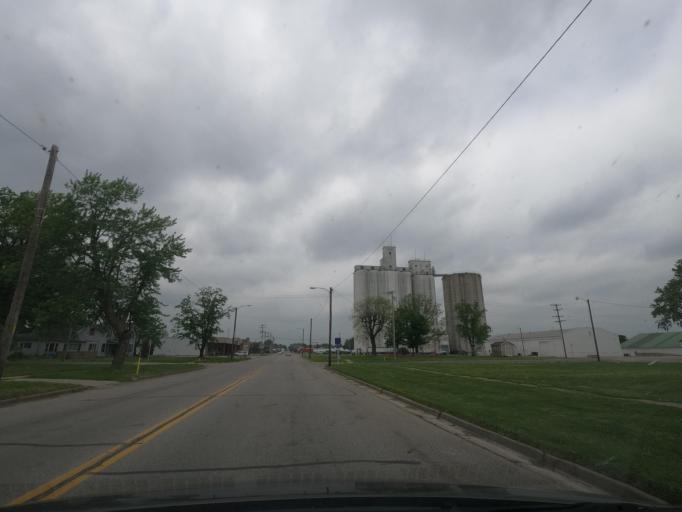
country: US
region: Kansas
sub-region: Cherokee County
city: Columbus
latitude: 37.1709
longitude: -94.8355
